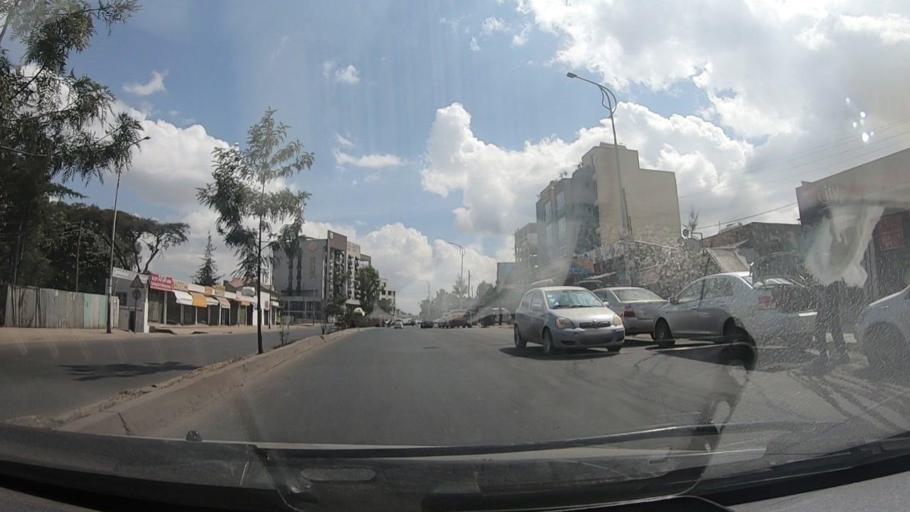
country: ET
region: Adis Abeba
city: Addis Ababa
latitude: 8.9811
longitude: 38.7204
